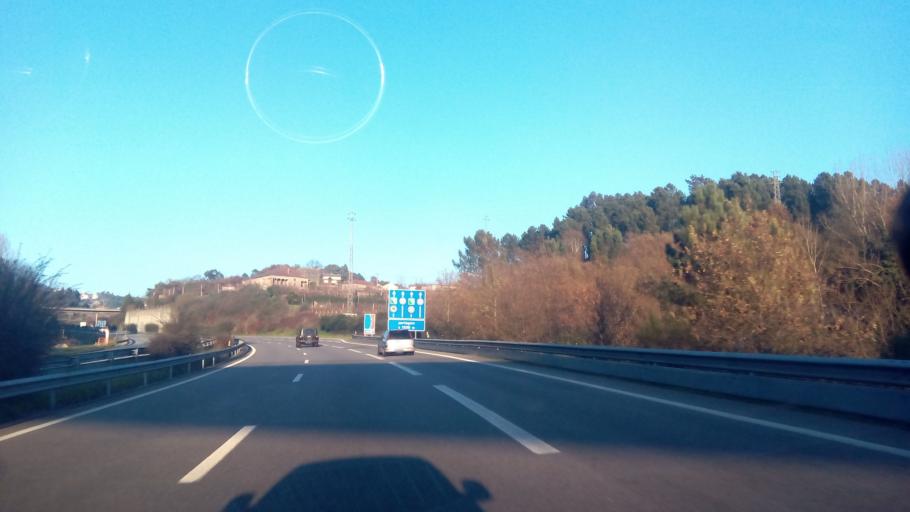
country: PT
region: Porto
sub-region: Marco de Canaveses
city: Marco de Canavezes
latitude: 41.2196
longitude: -8.1506
